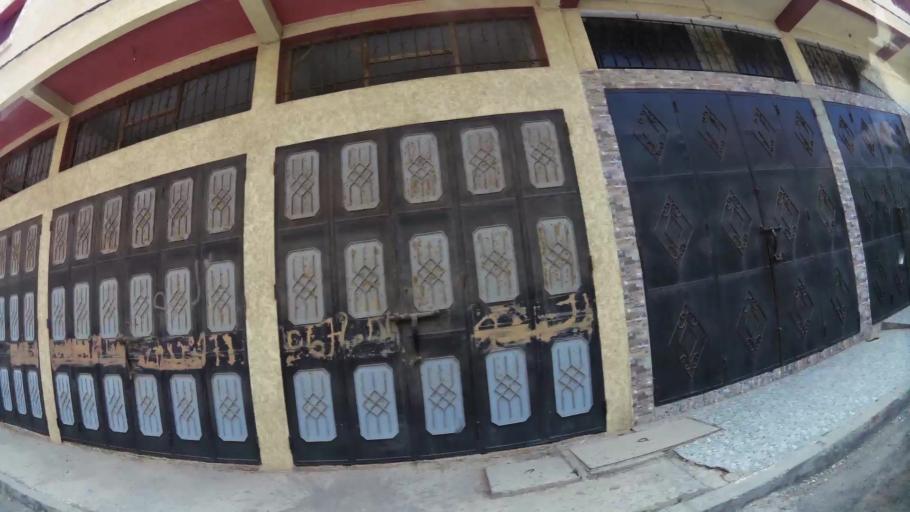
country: MA
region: Rabat-Sale-Zemmour-Zaer
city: Sale
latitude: 34.0707
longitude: -6.7920
